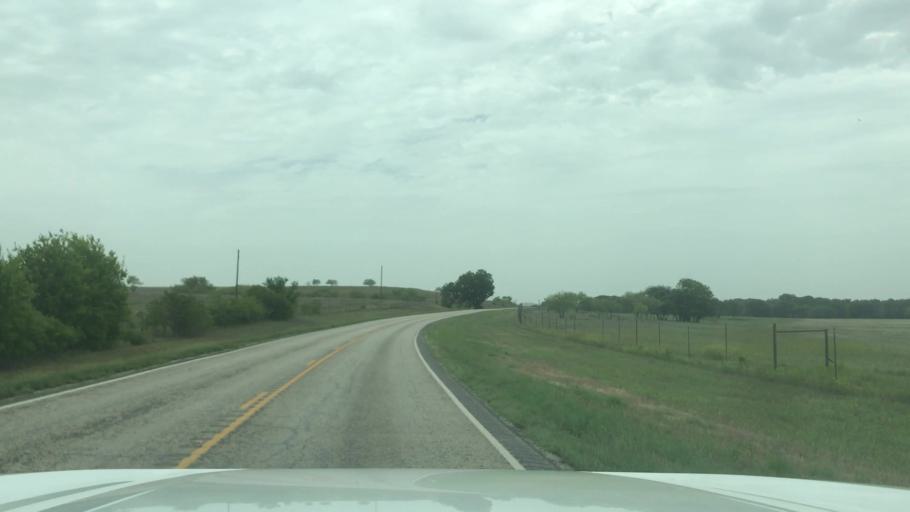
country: US
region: Texas
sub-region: Erath County
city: Dublin
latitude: 32.0574
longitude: -98.1878
